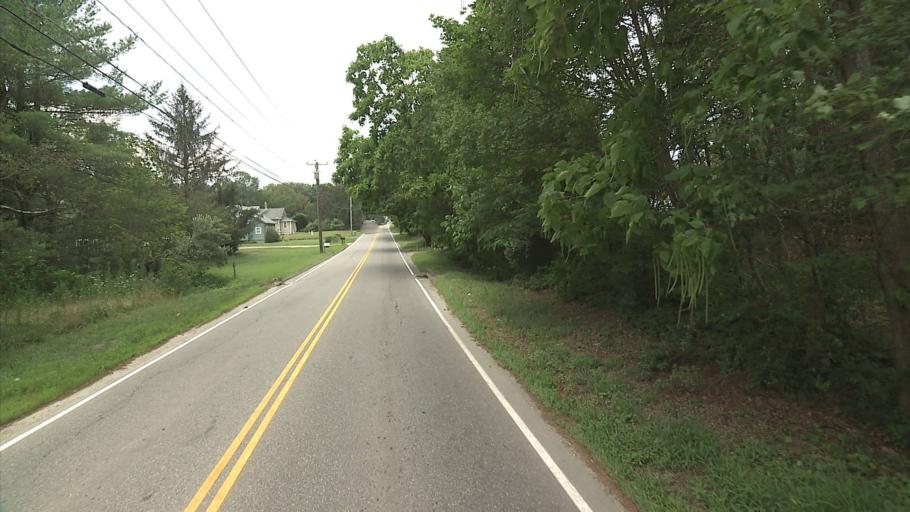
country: US
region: Connecticut
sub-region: Windham County
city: Wauregan
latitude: 41.7529
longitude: -71.9209
